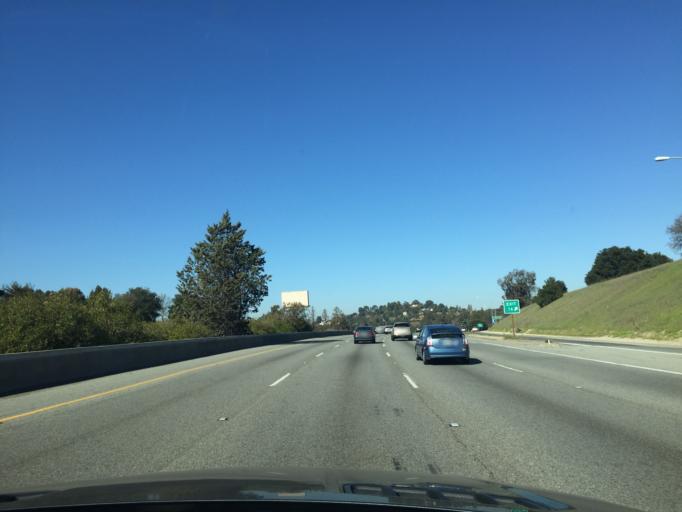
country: US
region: California
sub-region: Santa Clara County
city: Loyola
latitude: 37.3580
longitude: -122.1178
